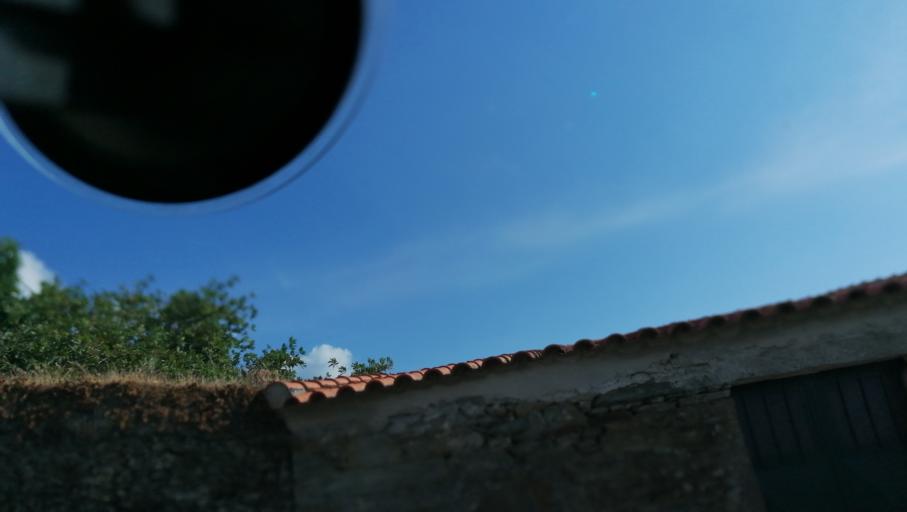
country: PT
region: Vila Real
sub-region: Sabrosa
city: Vilela
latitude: 41.2009
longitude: -7.5354
